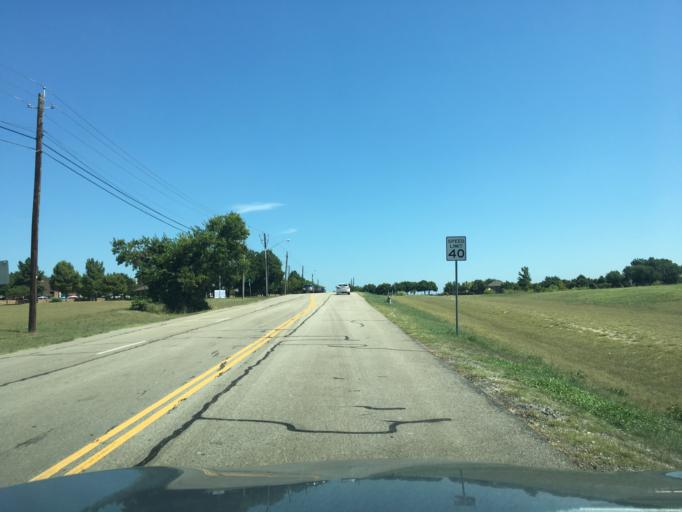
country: US
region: Texas
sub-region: Dallas County
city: Sachse
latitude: 32.9584
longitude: -96.6283
